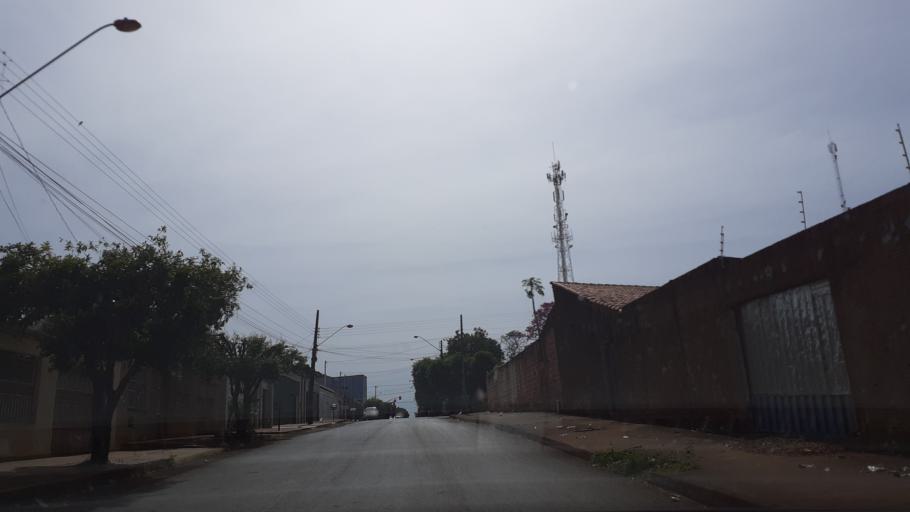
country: BR
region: Goias
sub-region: Itumbiara
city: Itumbiara
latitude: -18.4198
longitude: -49.2326
